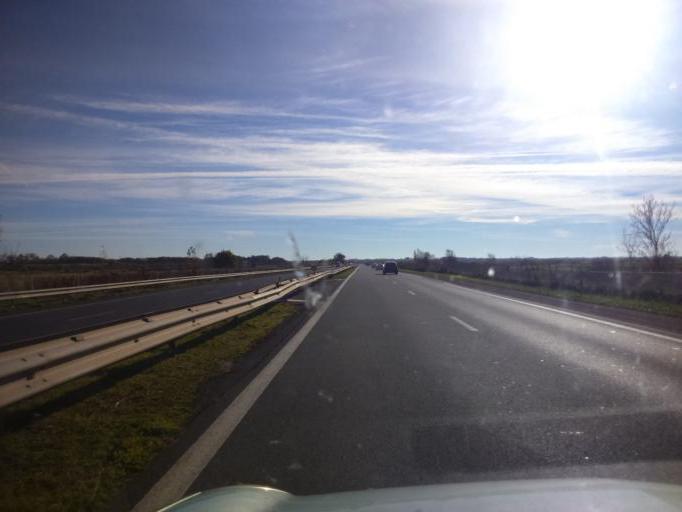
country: FR
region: Poitou-Charentes
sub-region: Departement de la Charente-Maritime
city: Saint-Laurent-de-la-Pree
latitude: 45.9858
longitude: -1.0273
